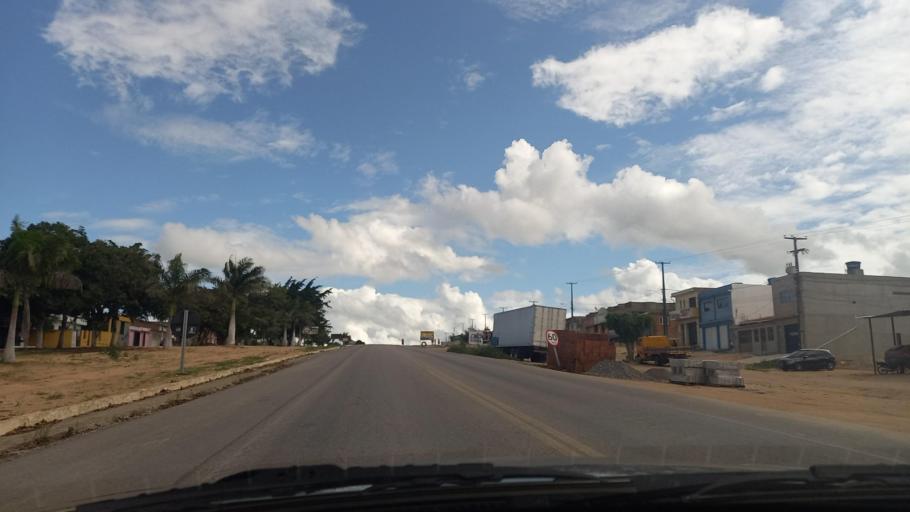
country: BR
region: Pernambuco
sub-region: Lajedo
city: Lajedo
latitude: -8.7120
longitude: -36.4202
